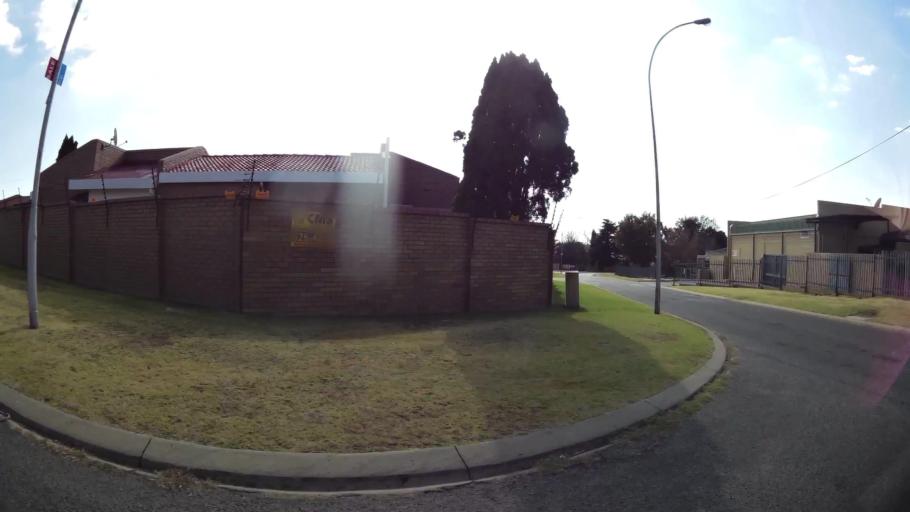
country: ZA
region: Gauteng
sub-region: Ekurhuleni Metropolitan Municipality
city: Benoni
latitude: -26.1355
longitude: 28.3482
